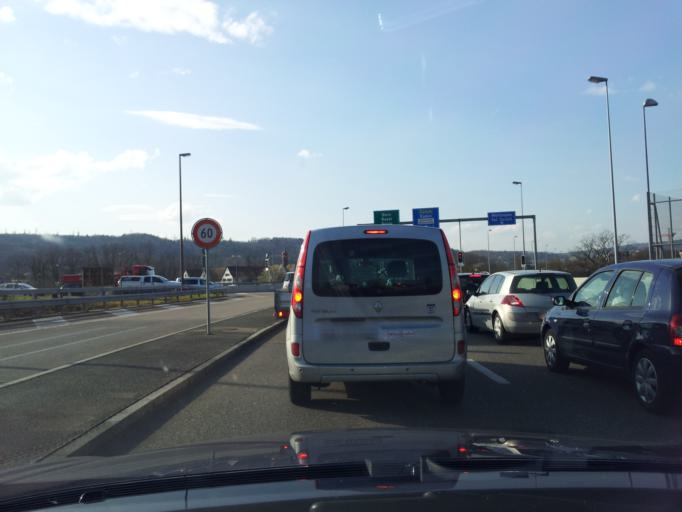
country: CH
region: Aargau
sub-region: Bezirk Baden
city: Neuenhof
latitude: 47.4542
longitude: 8.3209
